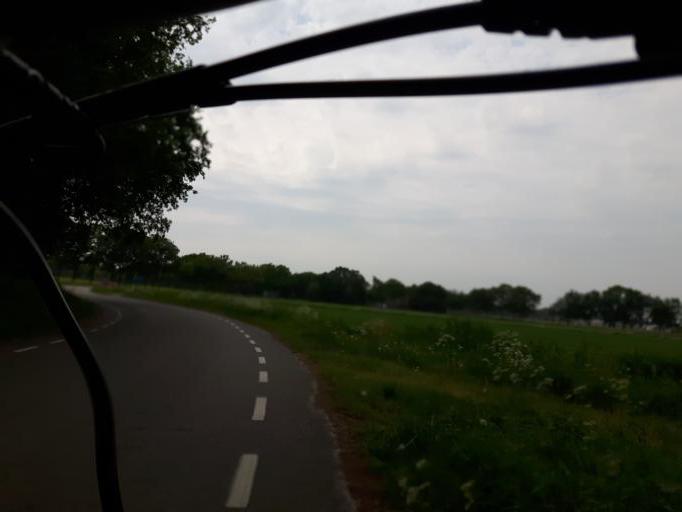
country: NL
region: North Brabant
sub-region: Gemeente Bergen op Zoom
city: Lepelstraat
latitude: 51.5309
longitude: 4.2991
